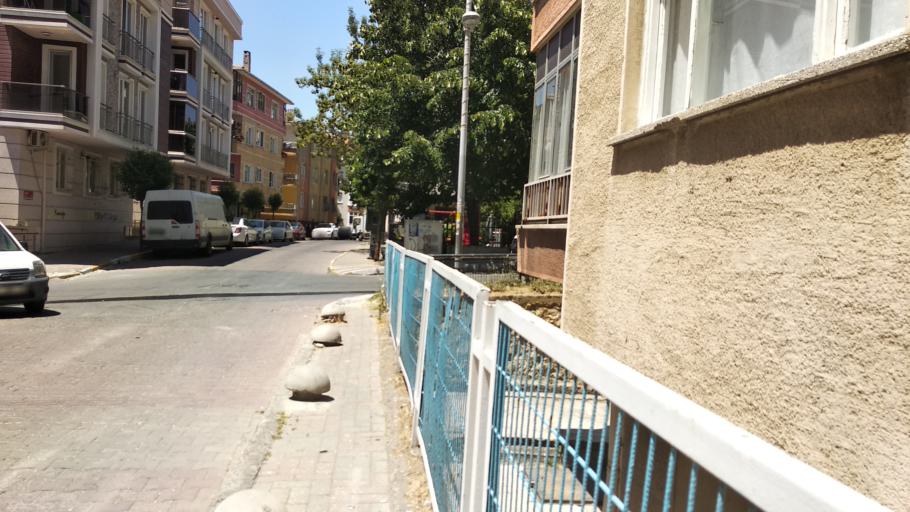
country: TR
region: Istanbul
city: Yakuplu
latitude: 40.9743
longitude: 28.7200
